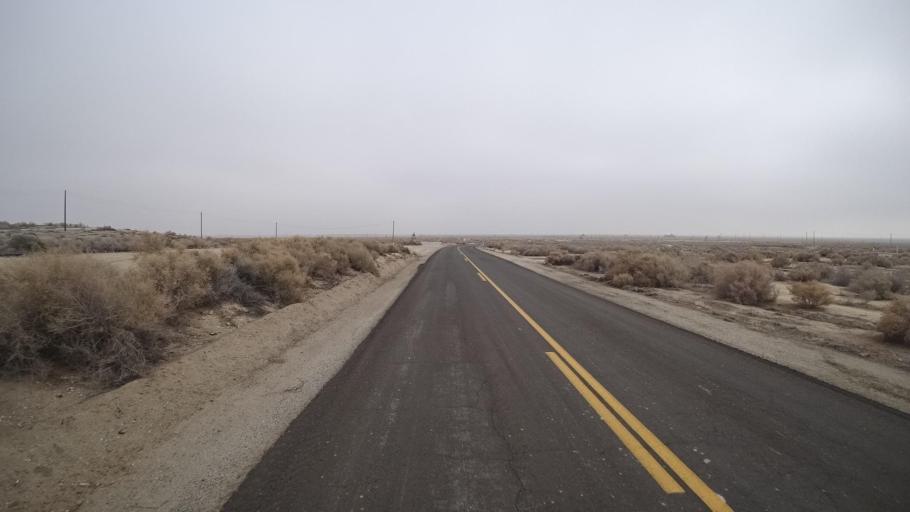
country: US
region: California
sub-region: Kern County
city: Maricopa
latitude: 35.0755
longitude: -119.3588
